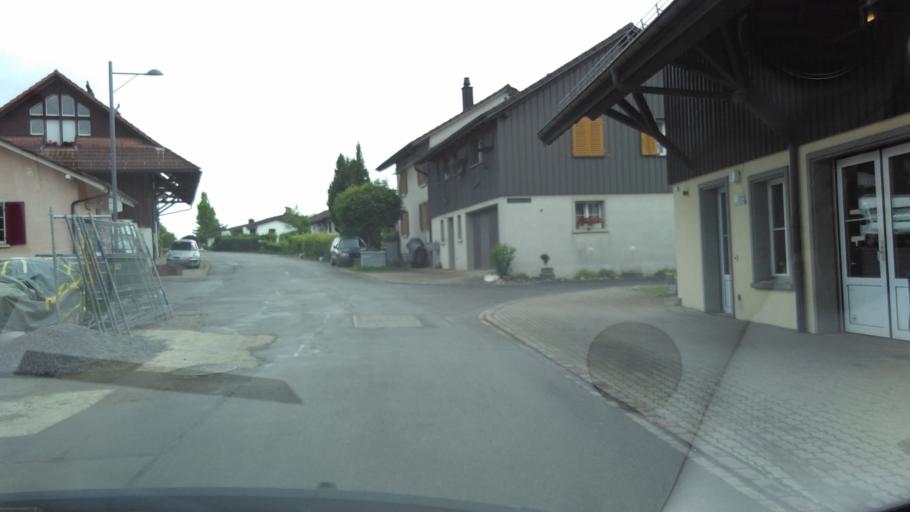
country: CH
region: Aargau
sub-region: Bezirk Bremgarten
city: Rudolfstetten
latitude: 47.3630
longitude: 8.3882
